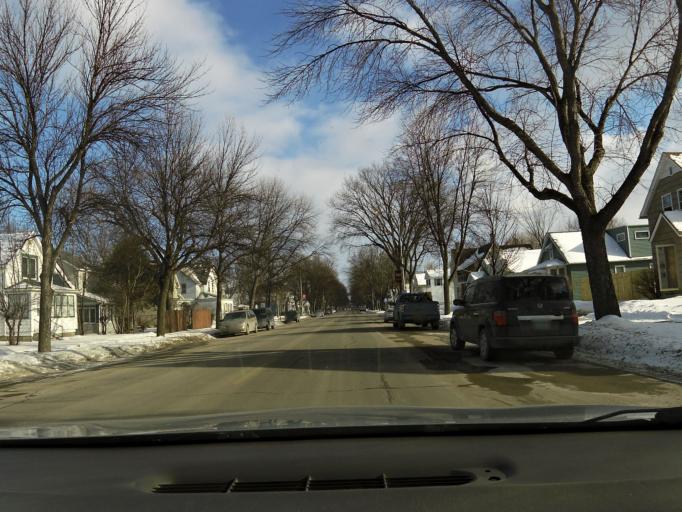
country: US
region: North Dakota
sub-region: Grand Forks County
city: Grand Forks
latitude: 47.9299
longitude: -97.0434
